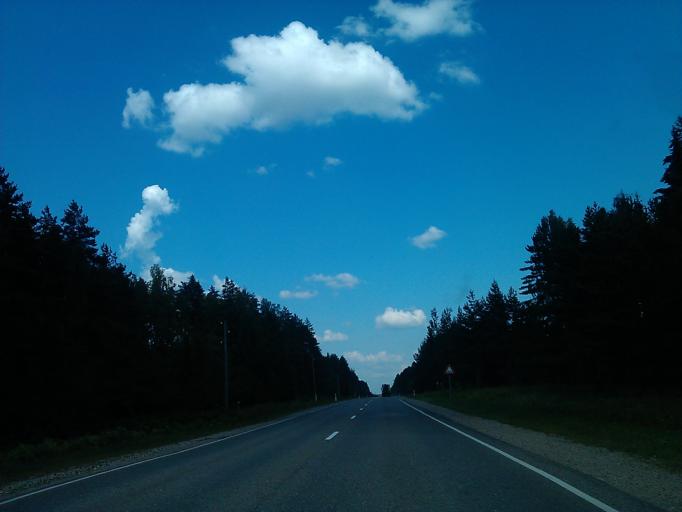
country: LV
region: Skrunda
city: Skrunda
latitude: 56.6595
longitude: 21.9455
